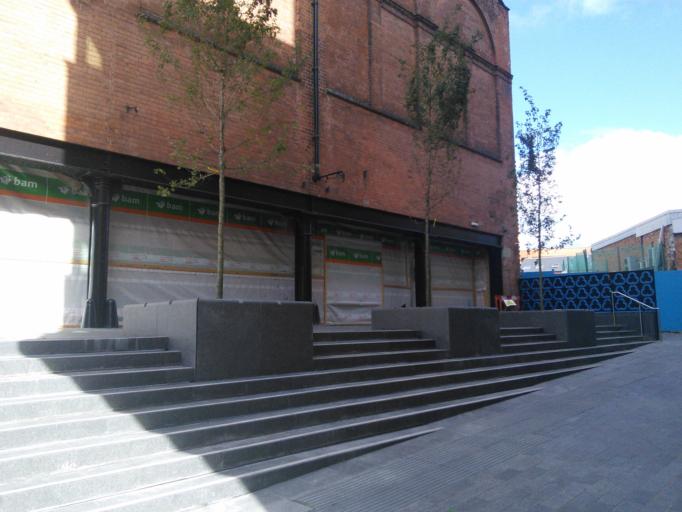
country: GB
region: England
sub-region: City and Borough of Birmingham
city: Birmingham
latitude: 52.4763
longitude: -1.8916
